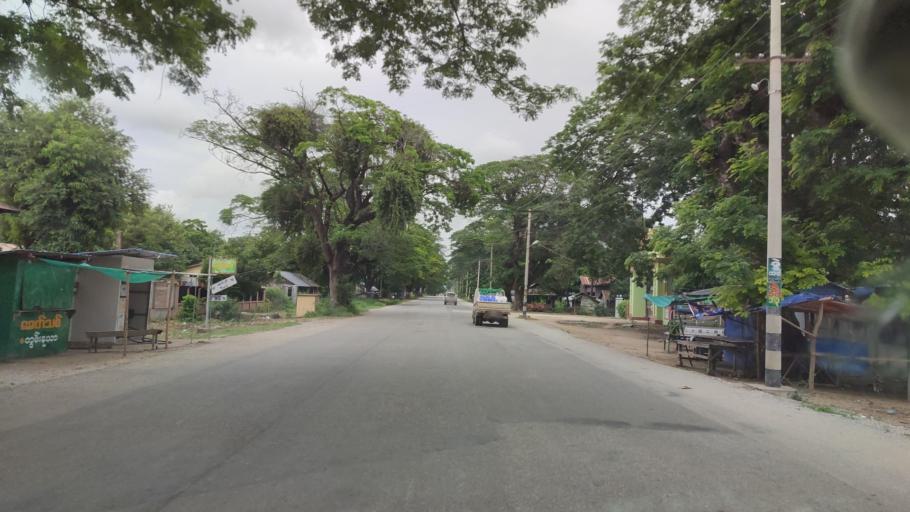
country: MM
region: Mandalay
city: Meiktila
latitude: 20.9408
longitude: 95.9313
